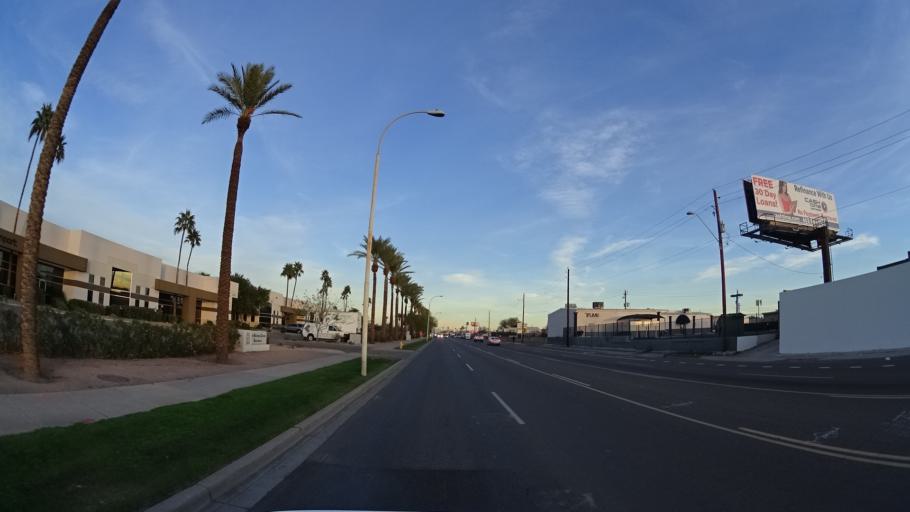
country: US
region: Arizona
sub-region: Maricopa County
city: Tempe Junction
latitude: 33.4220
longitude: -111.9984
